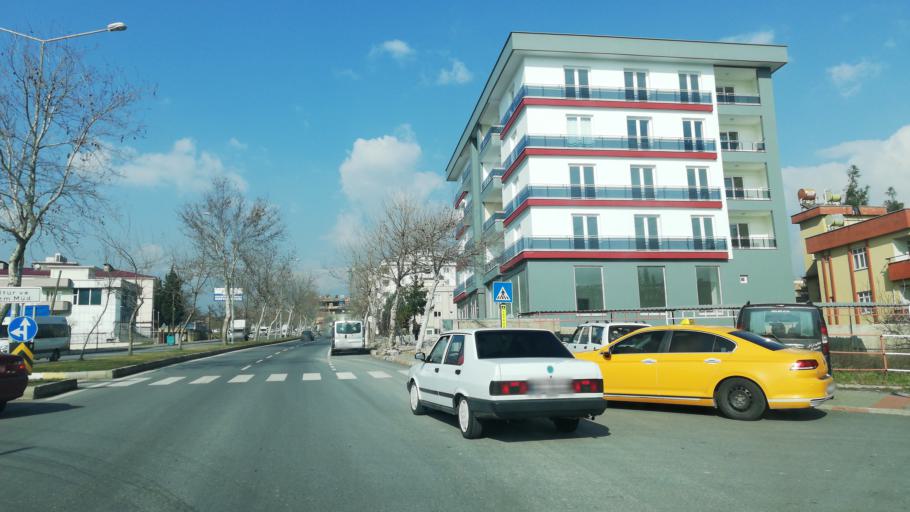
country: TR
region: Kahramanmaras
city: Kahramanmaras
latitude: 37.5678
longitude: 36.9423
